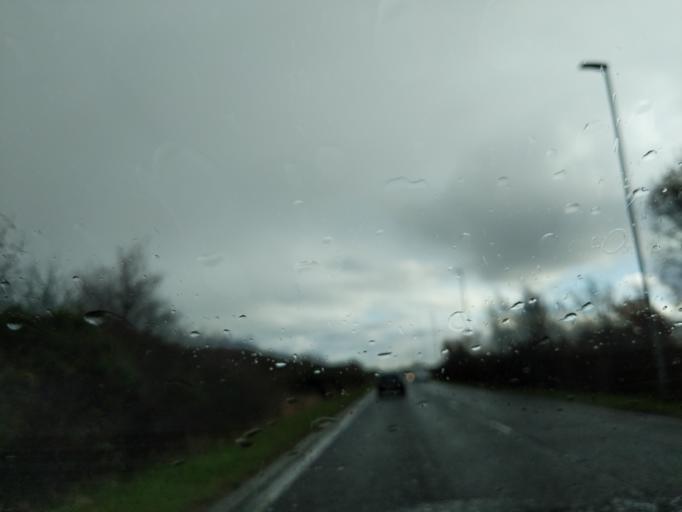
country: GB
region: England
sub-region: Northumberland
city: Seaton Delaval
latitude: 55.1031
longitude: -1.5367
